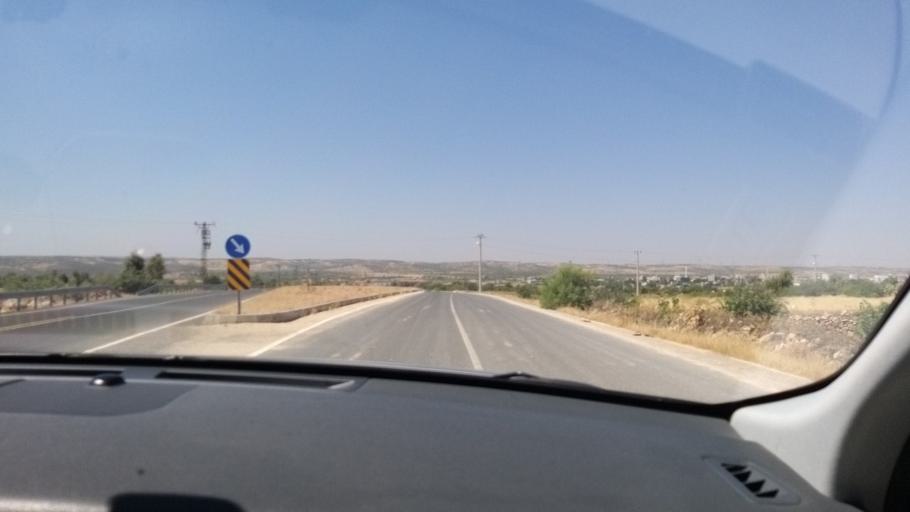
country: TR
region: Mardin
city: Dargecit
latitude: 37.5464
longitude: 41.7418
